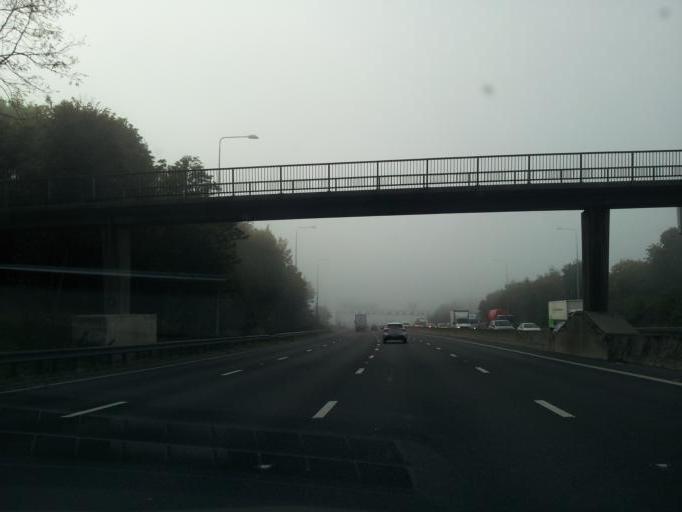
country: GB
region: England
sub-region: Kirklees
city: Cleckheaton
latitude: 53.7135
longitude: -1.7455
